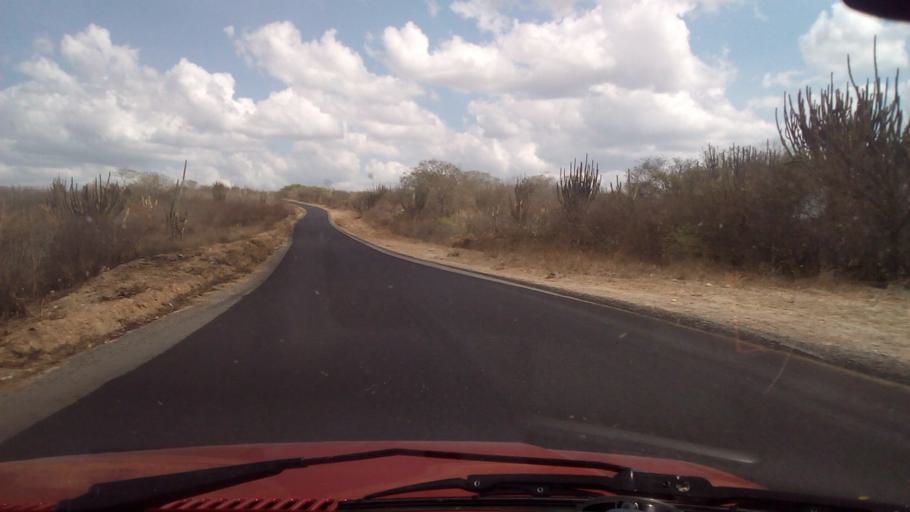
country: BR
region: Paraiba
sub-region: Bananeiras
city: Bananeiras
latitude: -6.7189
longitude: -35.7171
